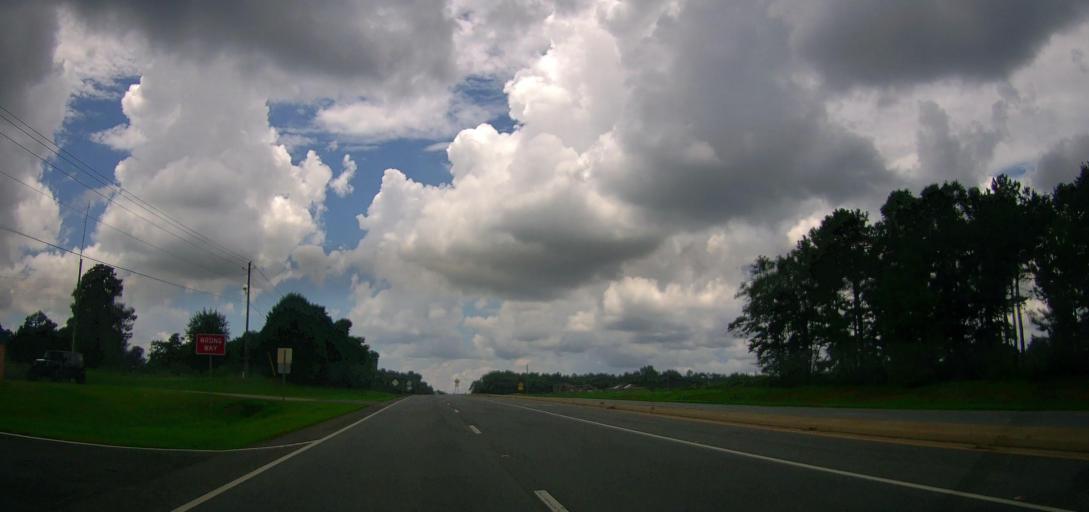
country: US
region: Georgia
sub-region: Pulaski County
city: Hawkinsville
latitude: 32.2965
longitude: -83.4877
